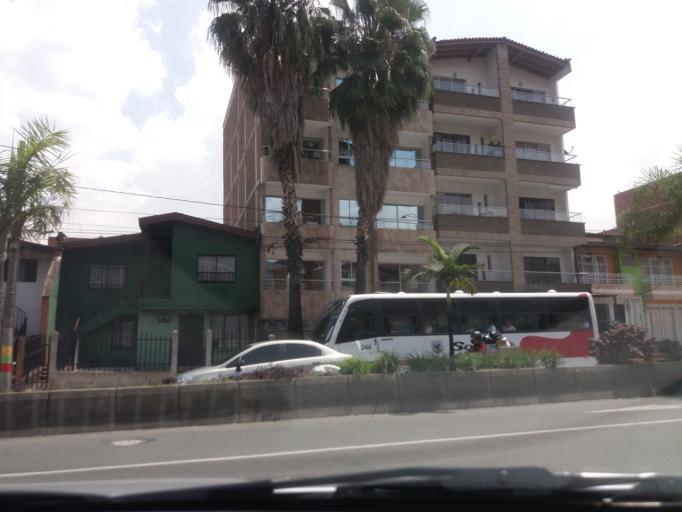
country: CO
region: Antioquia
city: Itagui
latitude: 6.1904
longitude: -75.5929
